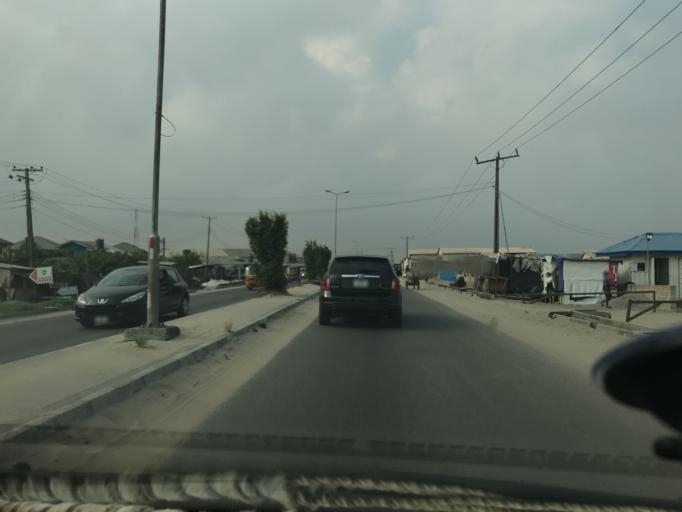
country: NG
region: Lagos
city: Ikoyi
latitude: 6.4852
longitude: 3.5752
